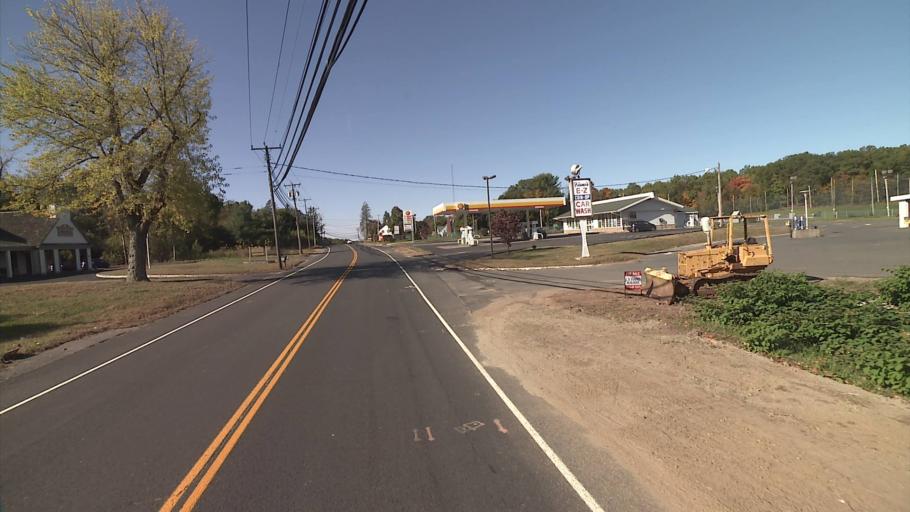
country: US
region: Connecticut
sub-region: Hartford County
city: Manchester
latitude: 41.7852
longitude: -72.4584
